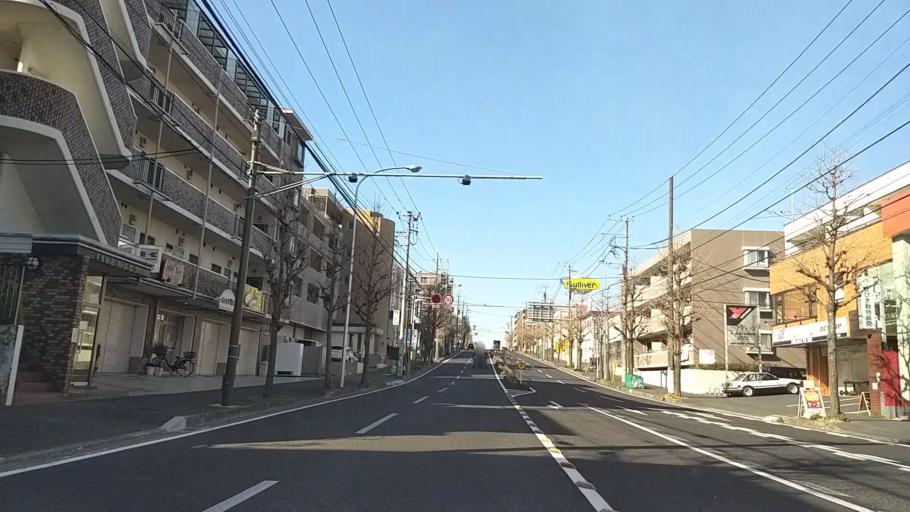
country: JP
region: Kanagawa
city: Kamakura
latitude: 35.3711
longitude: 139.5995
